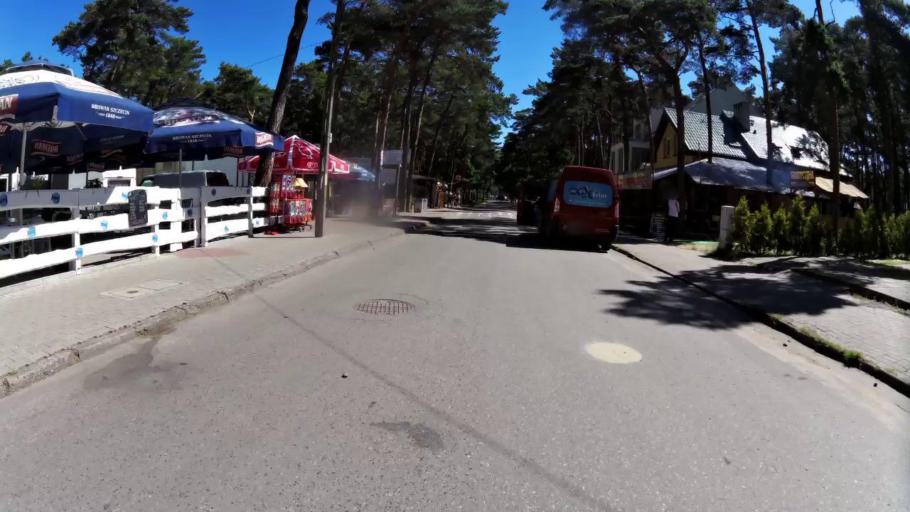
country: PL
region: West Pomeranian Voivodeship
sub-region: Powiat gryficki
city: Pobierowo
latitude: 54.0576
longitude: 14.9191
